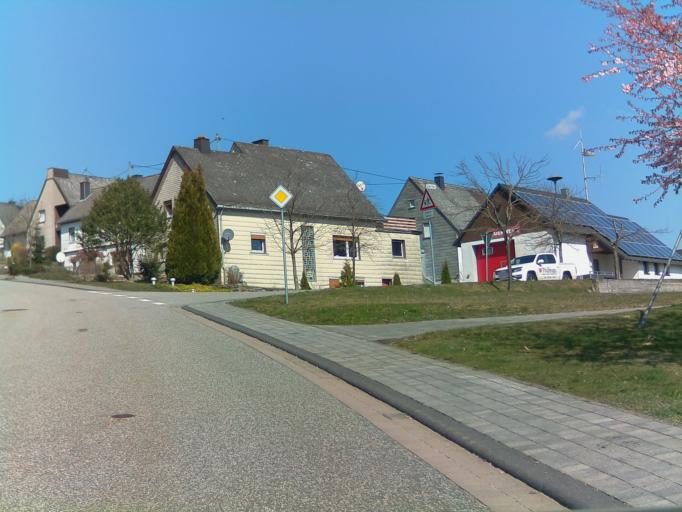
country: DE
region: Rheinland-Pfalz
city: Hattgenstein
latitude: 49.6980
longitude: 7.1585
